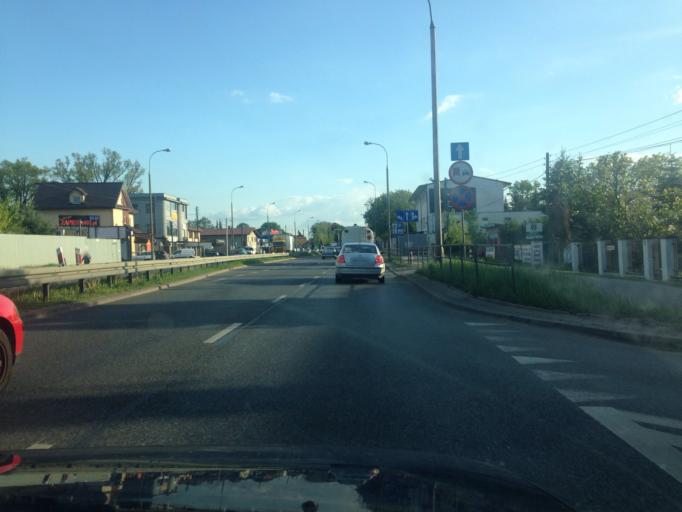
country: PL
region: Masovian Voivodeship
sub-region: Powiat wolominski
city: Marki
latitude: 52.3426
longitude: 21.1210
